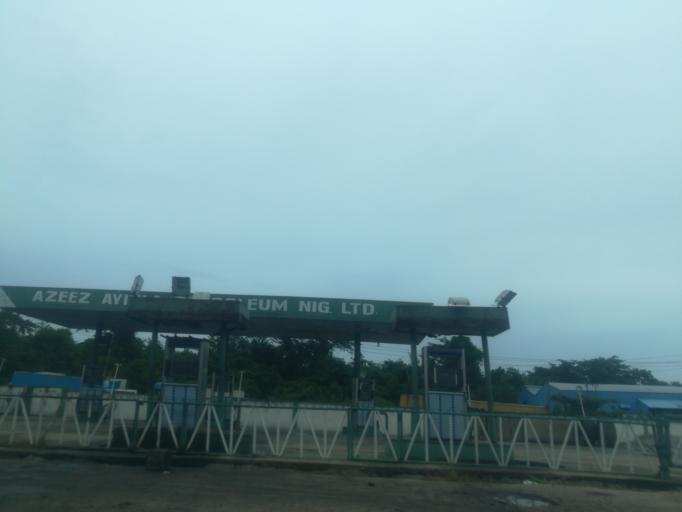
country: NG
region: Oyo
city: Ibadan
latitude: 7.3331
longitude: 3.8815
